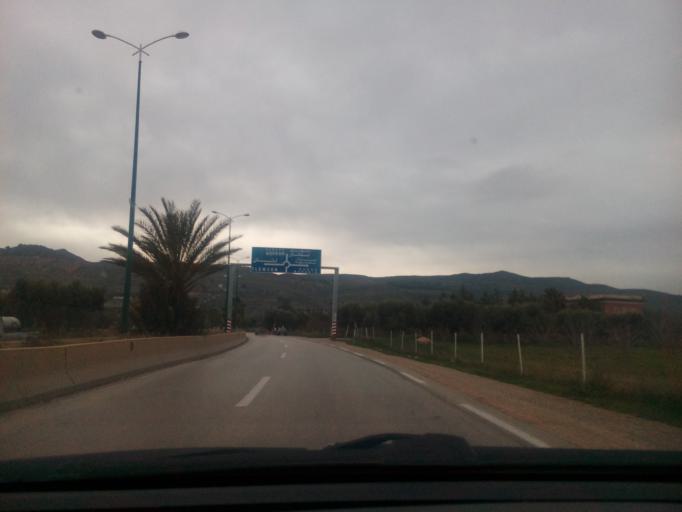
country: DZ
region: Tlemcen
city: Mansoura
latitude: 34.8693
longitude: -1.3500
